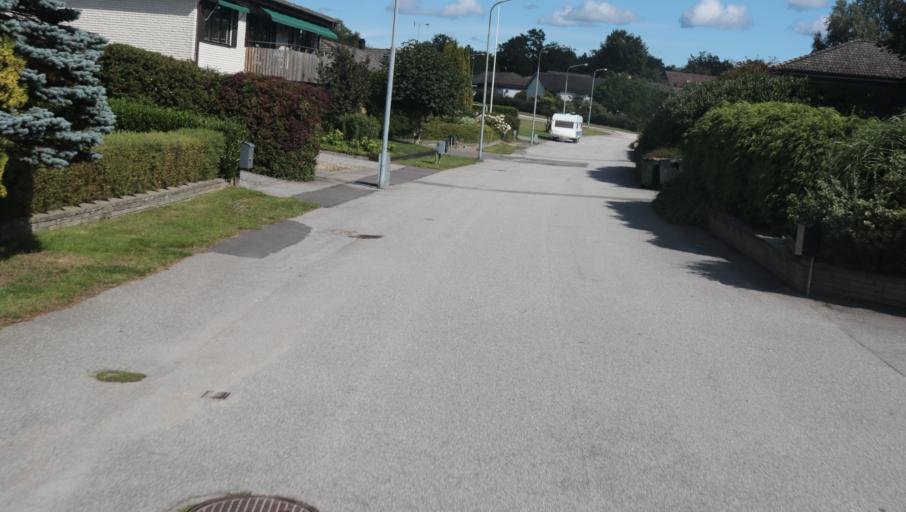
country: SE
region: Blekinge
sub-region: Karlshamns Kommun
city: Karlshamn
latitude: 56.1873
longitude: 14.8666
